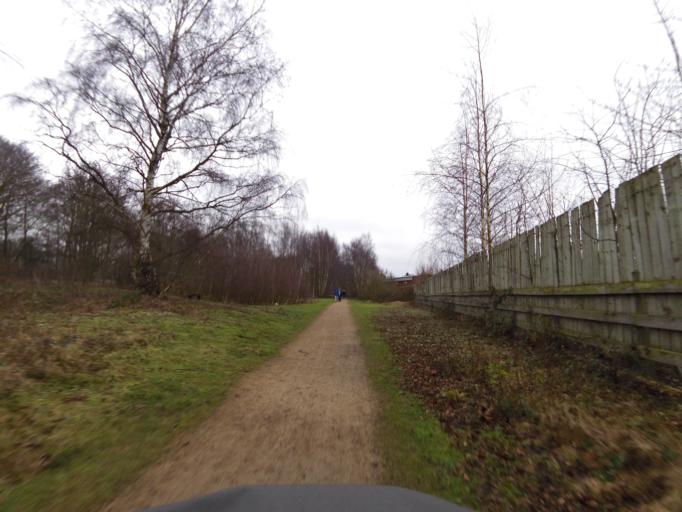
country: GB
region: England
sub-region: Norfolk
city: Mattishall
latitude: 52.7225
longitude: 1.1161
